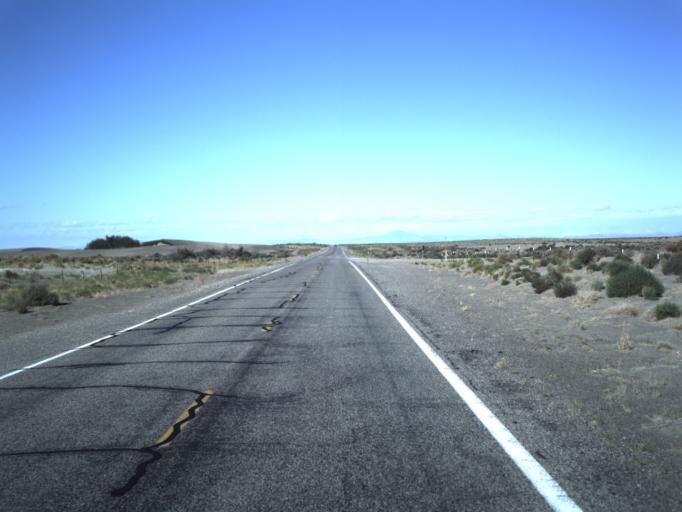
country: US
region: Utah
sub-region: Millard County
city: Delta
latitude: 39.3546
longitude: -112.3983
